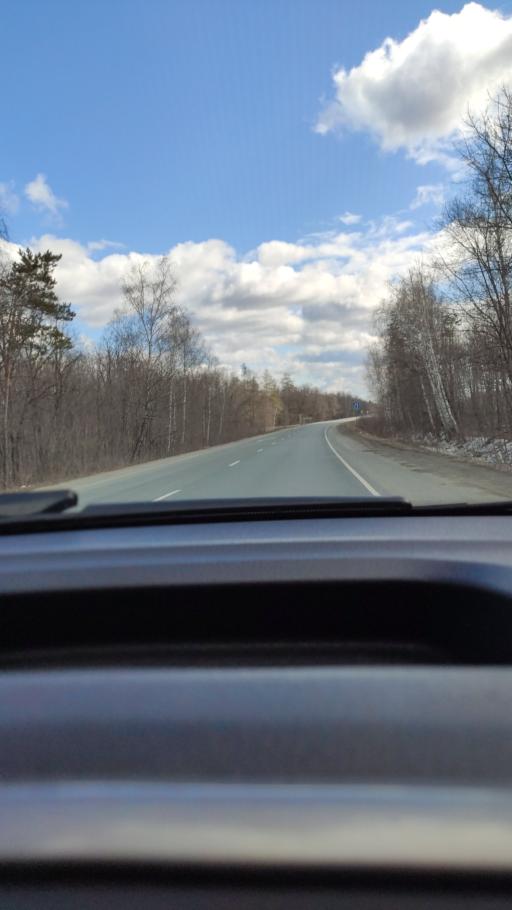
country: RU
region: Samara
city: Pribrezhnyy
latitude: 53.5112
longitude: 49.9270
